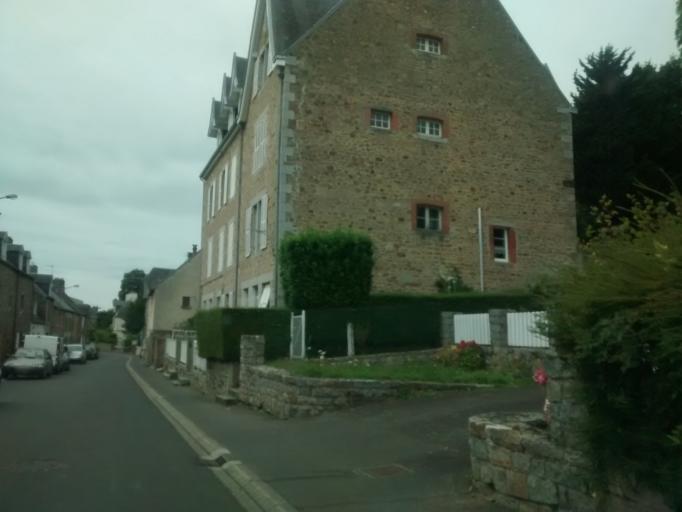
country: FR
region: Lower Normandy
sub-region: Departement de la Manche
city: Sartilly
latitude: 48.7304
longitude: -1.5161
